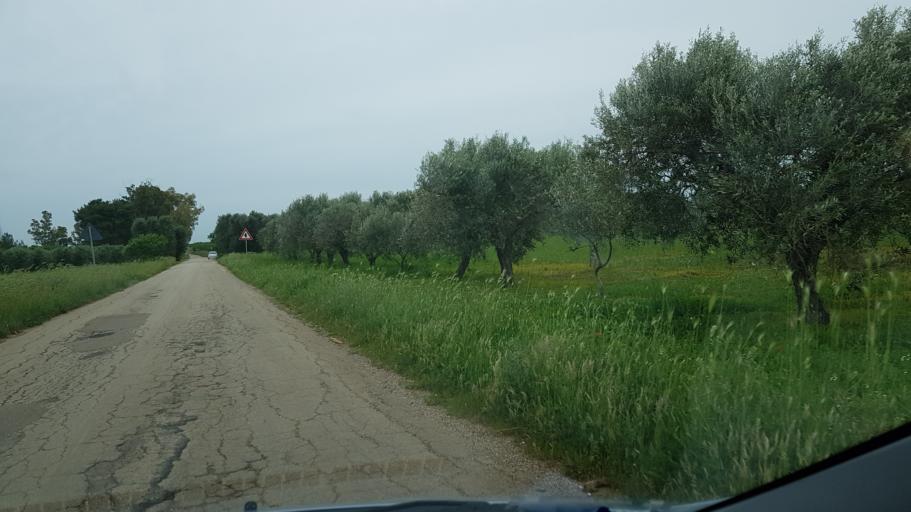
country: IT
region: Apulia
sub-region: Provincia di Brindisi
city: Mesagne
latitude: 40.6206
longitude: 17.7717
